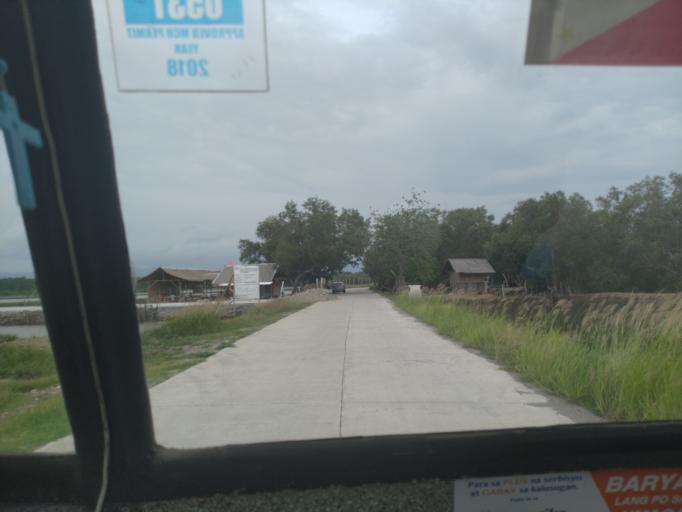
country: PH
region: Central Visayas
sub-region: Province of Negros Oriental
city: Tanjay
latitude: 9.5422
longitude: 123.1539
